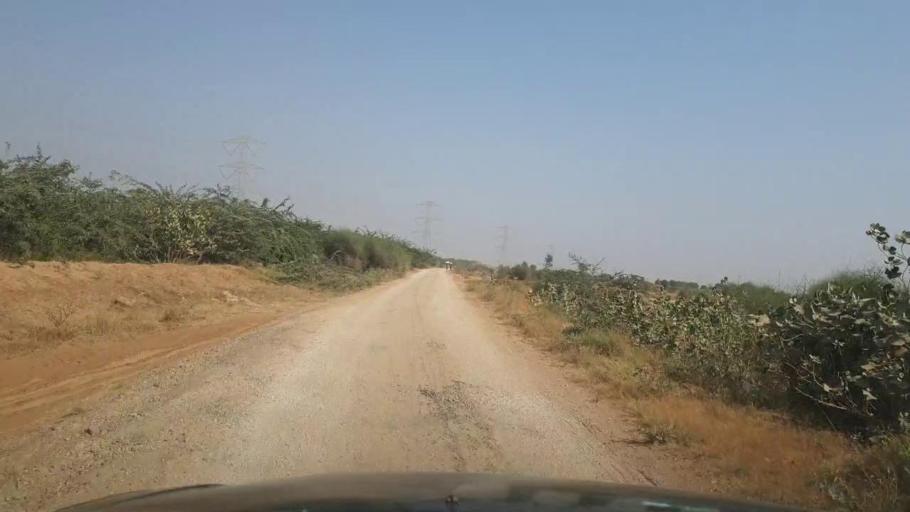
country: PK
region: Sindh
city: Gharo
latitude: 25.2315
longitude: 67.6785
